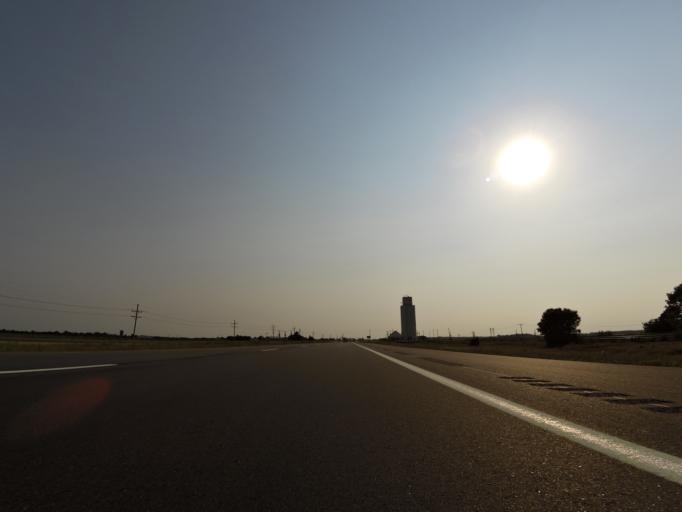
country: US
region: Kansas
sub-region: Reno County
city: South Hutchinson
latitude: 38.0089
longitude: -98.0112
